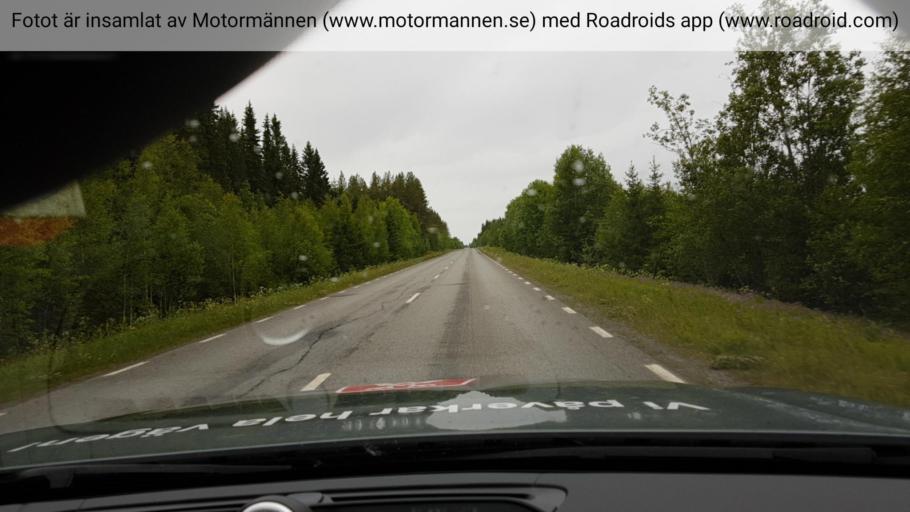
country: SE
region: Jaemtland
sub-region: Stroemsunds Kommun
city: Stroemsund
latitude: 63.6126
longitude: 15.2796
